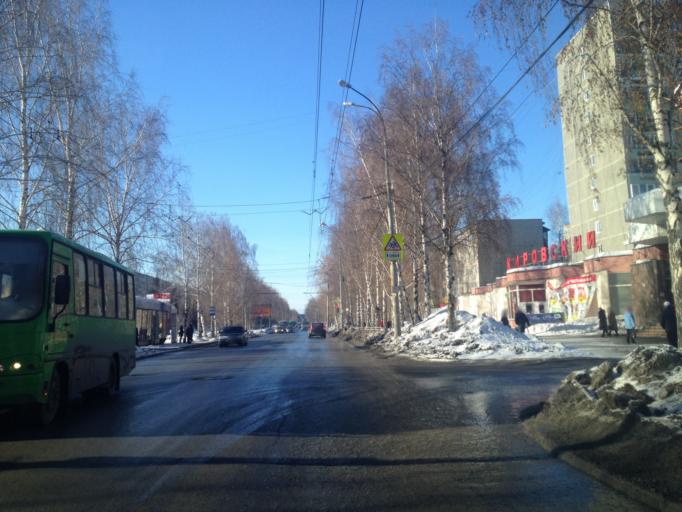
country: RU
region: Sverdlovsk
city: Sovkhoznyy
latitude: 56.7990
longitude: 60.5760
